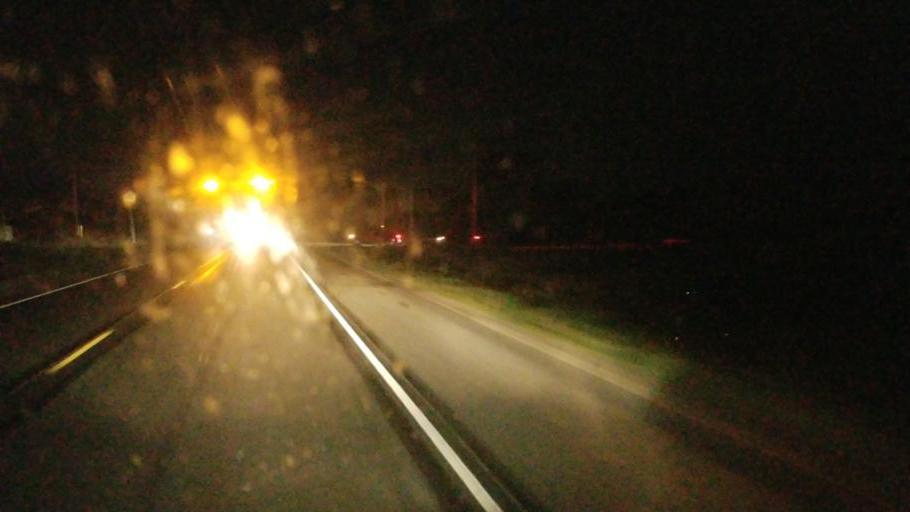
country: US
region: Indiana
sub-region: Elkhart County
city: Middlebury
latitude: 41.6543
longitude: -85.6184
